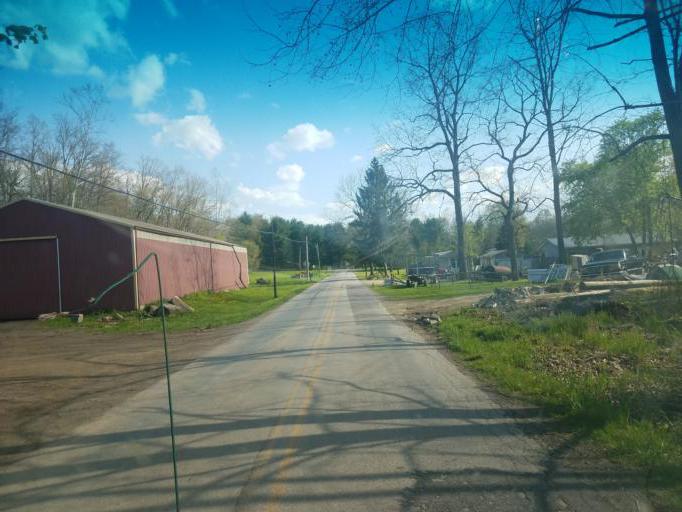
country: US
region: Ohio
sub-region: Wayne County
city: Apple Creek
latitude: 40.7938
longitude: -81.8769
